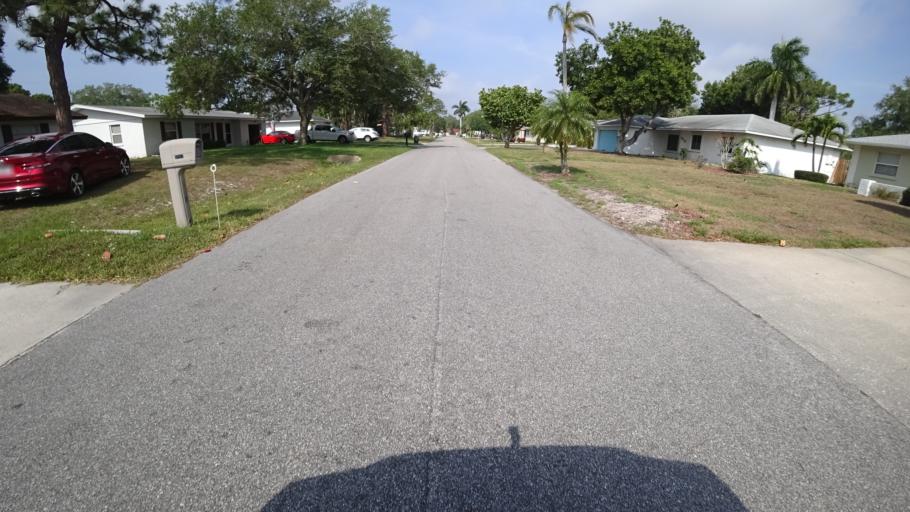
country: US
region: Florida
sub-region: Manatee County
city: West Bradenton
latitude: 27.4890
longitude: -82.6135
